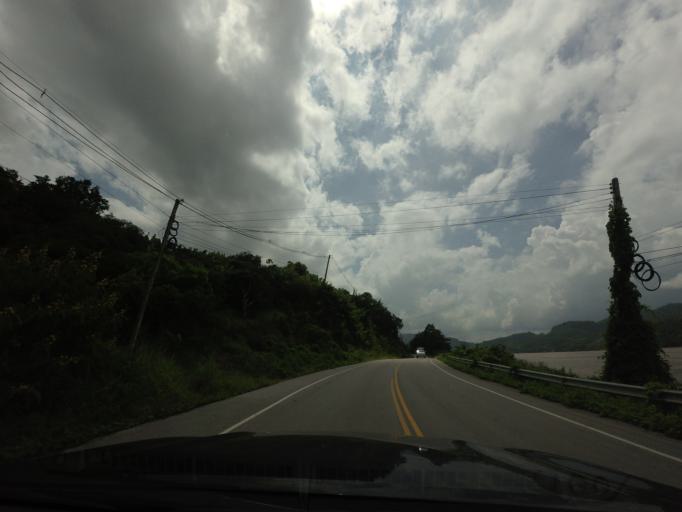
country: TH
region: Loei
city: Pak Chom
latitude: 18.0463
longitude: 101.7736
